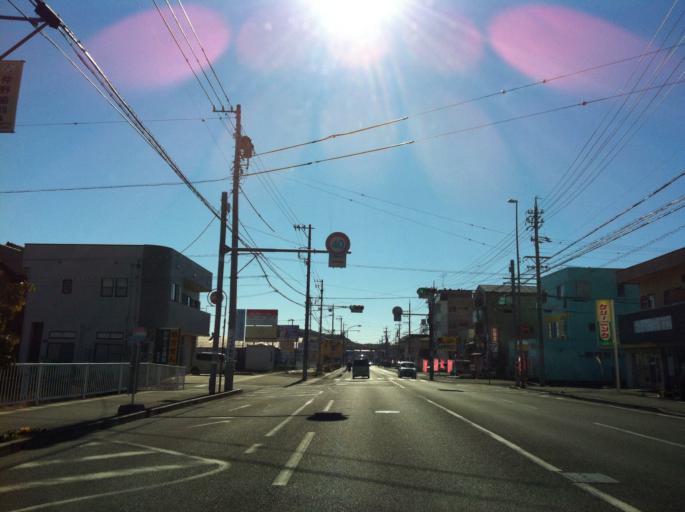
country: JP
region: Shizuoka
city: Shizuoka-shi
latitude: 35.0018
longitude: 138.3916
